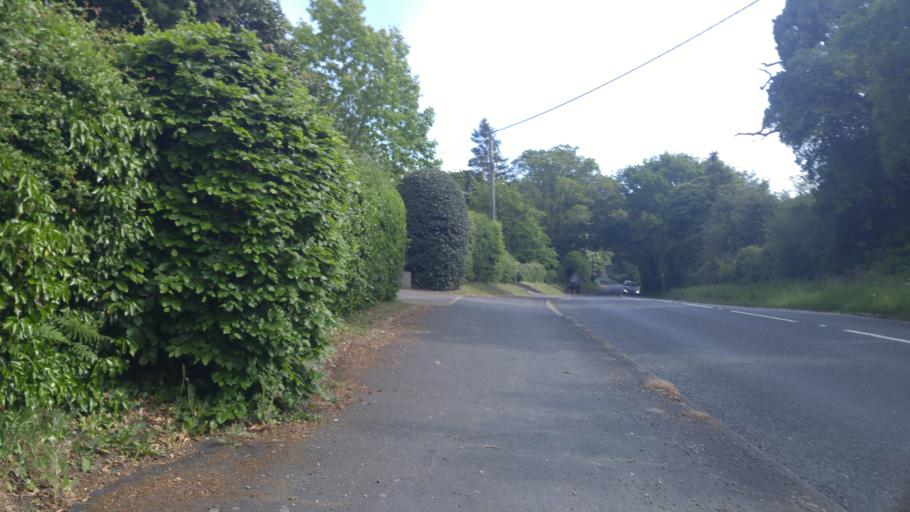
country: GB
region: England
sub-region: Essex
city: Layer de la Haye
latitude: 51.8559
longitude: 0.8662
